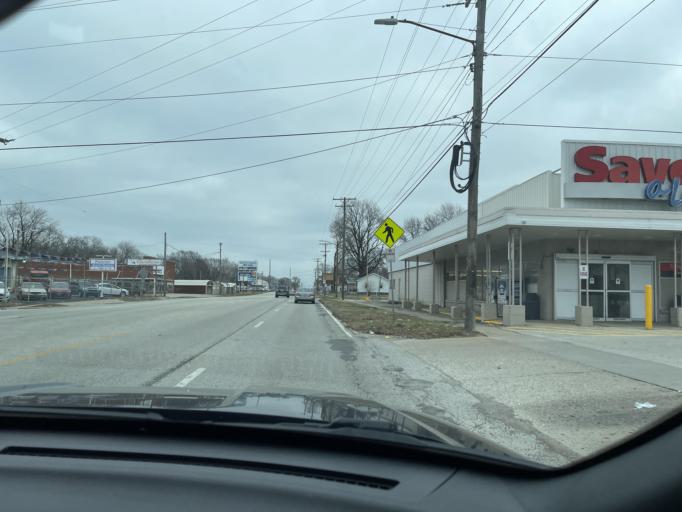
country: US
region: Illinois
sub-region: Sangamon County
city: Grandview
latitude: 39.8019
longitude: -89.6182
